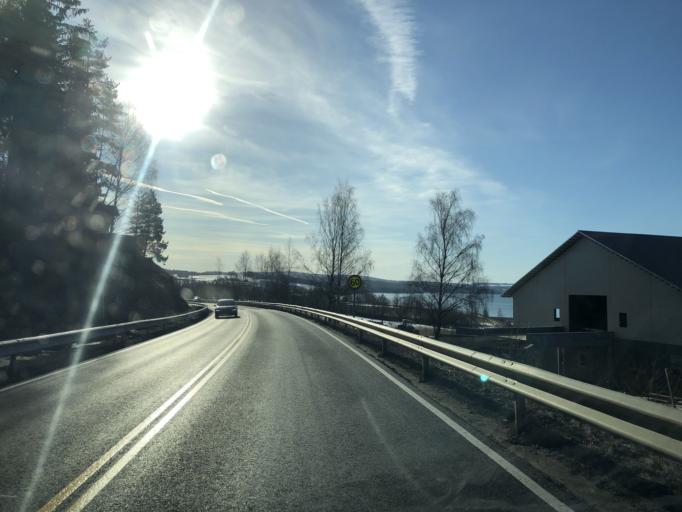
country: NO
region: Hedmark
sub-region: Ringsaker
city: Moelv
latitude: 60.9089
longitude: 10.7063
